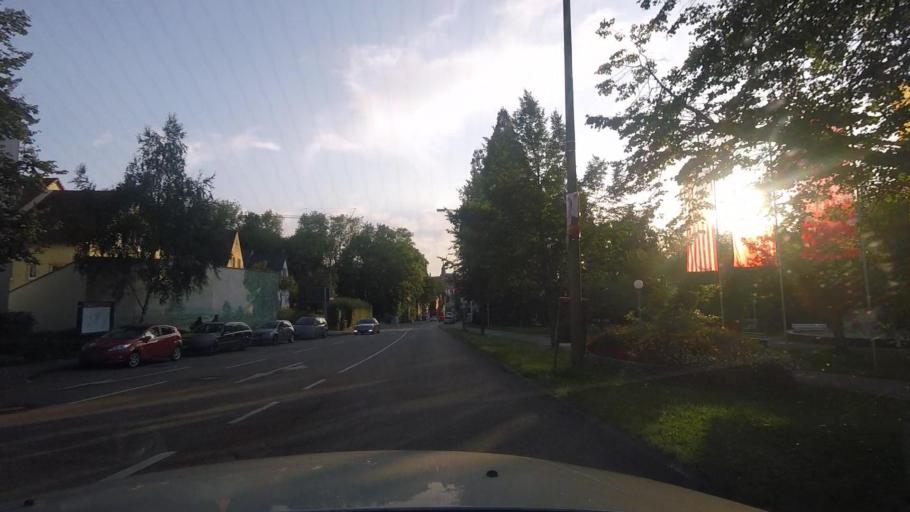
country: DE
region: Baden-Wuerttemberg
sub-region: Regierungsbezirk Stuttgart
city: Marbach am Neckar
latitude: 48.9427
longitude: 9.2640
